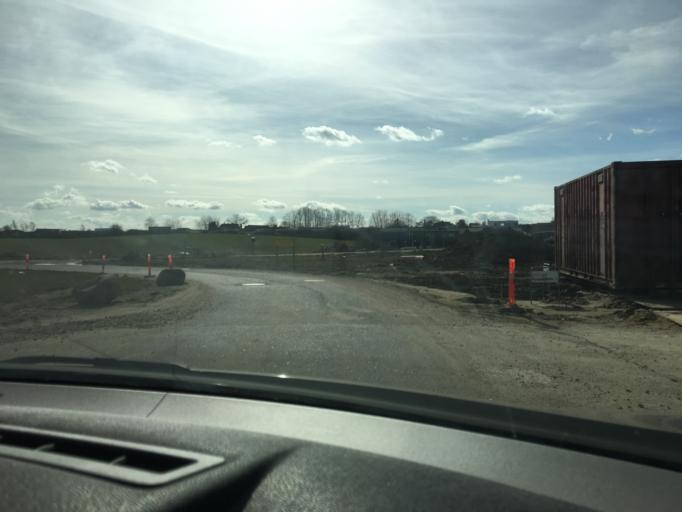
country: DK
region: South Denmark
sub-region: Vejle Kommune
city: Vejle
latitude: 55.7327
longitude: 9.6136
